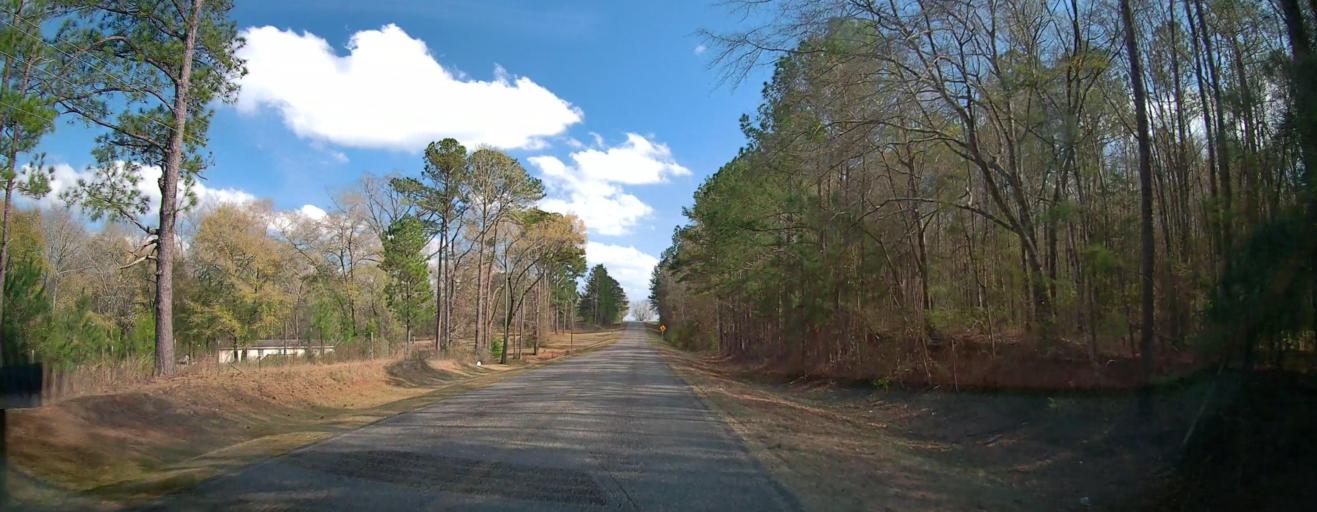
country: US
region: Georgia
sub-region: Twiggs County
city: Jeffersonville
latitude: 32.6584
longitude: -83.2222
